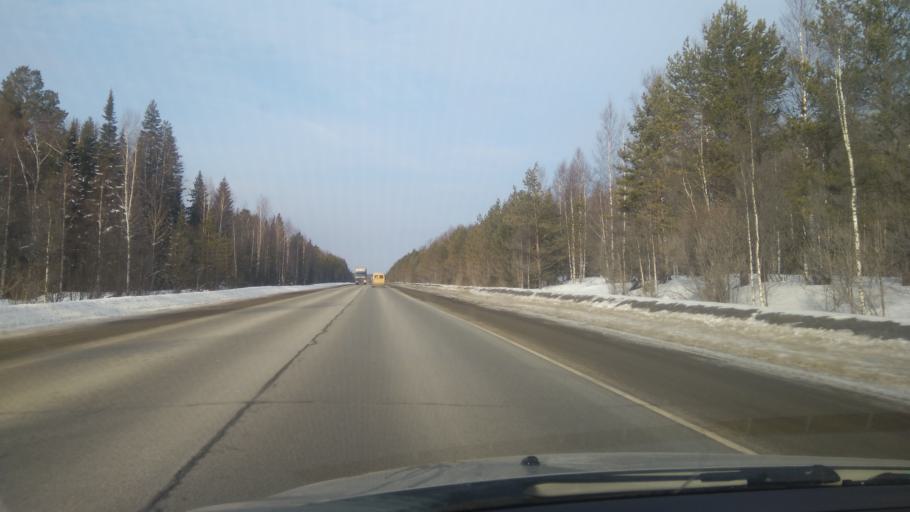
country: RU
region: Sverdlovsk
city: Nizhniye Sergi
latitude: 56.8242
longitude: 59.2877
